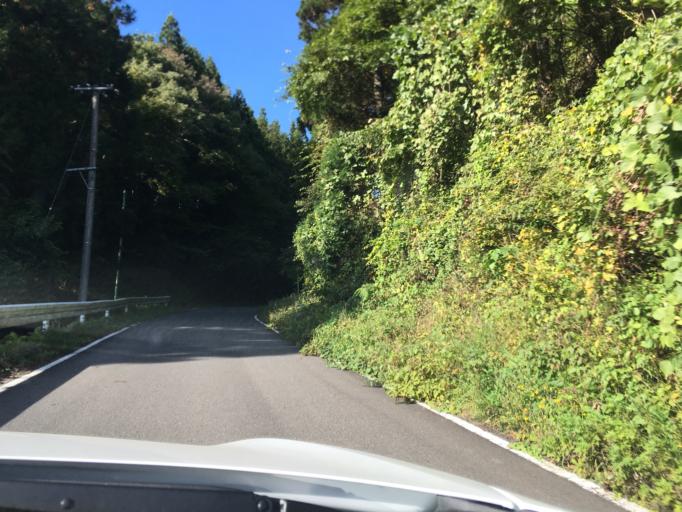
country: JP
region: Fukushima
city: Ishikawa
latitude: 37.1343
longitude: 140.5454
